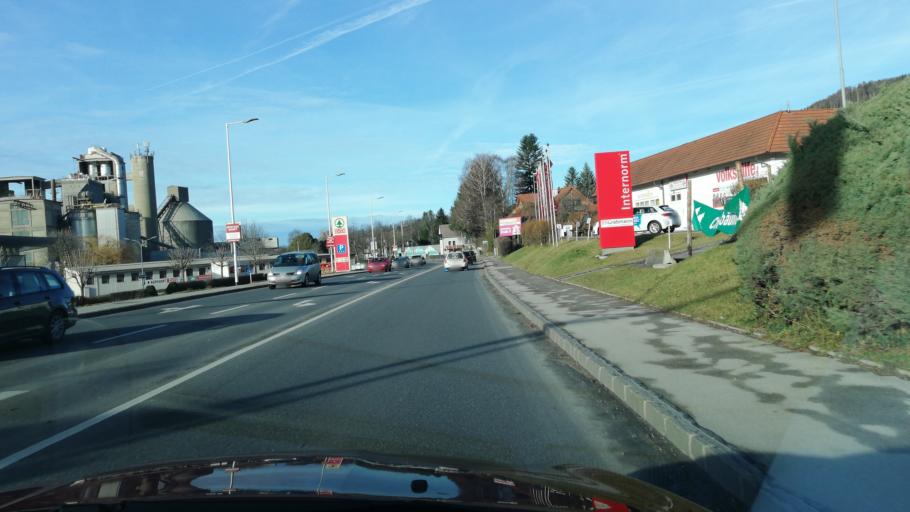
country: AT
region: Upper Austria
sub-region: Politischer Bezirk Kirchdorf an der Krems
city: Micheldorf in Oberoesterreich
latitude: 47.9066
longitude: 14.1195
